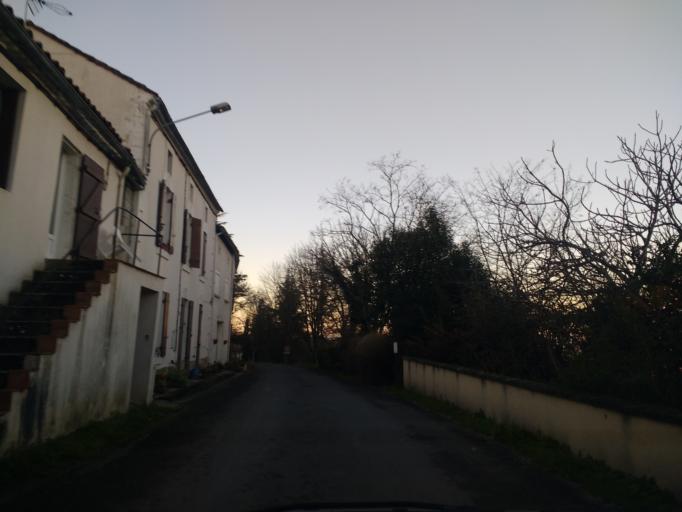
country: FR
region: Aquitaine
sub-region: Departement du Lot-et-Garonne
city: Castelmoron-sur-Lot
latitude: 44.3479
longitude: 0.5230
